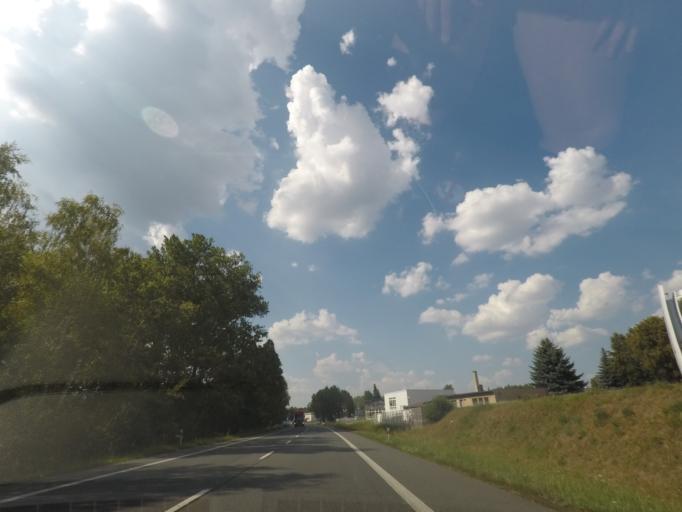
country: CZ
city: Tyniste nad Orlici
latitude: 50.1553
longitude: 16.0663
